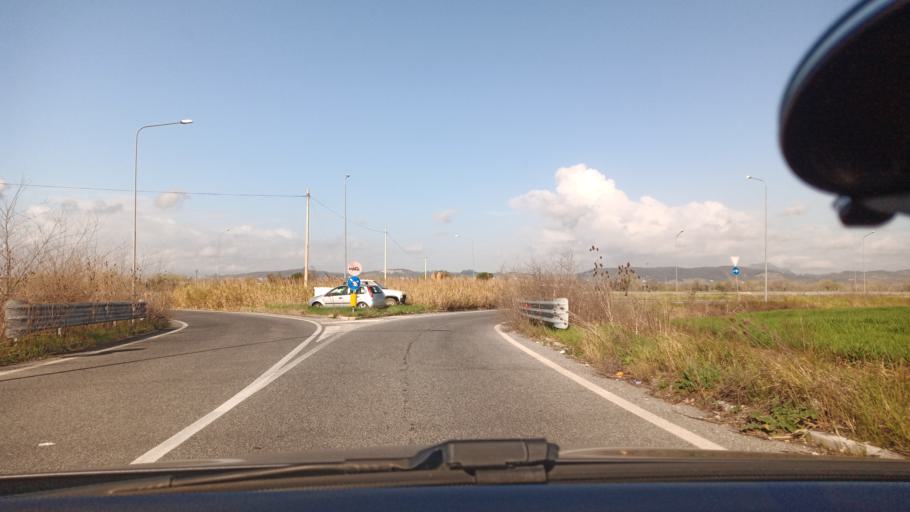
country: IT
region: Latium
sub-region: Citta metropolitana di Roma Capitale
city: Fiano Romano
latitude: 42.1570
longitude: 12.6438
